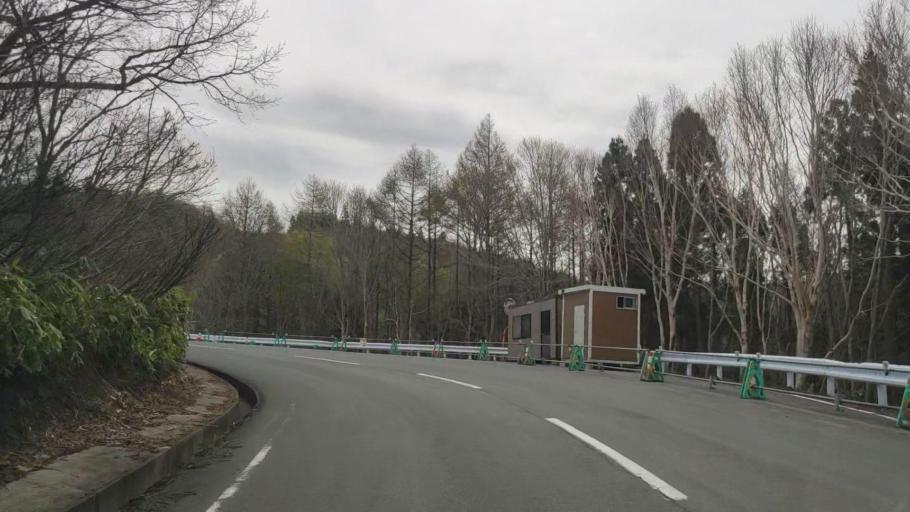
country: JP
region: Aomori
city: Aomori Shi
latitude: 40.7176
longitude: 140.8665
